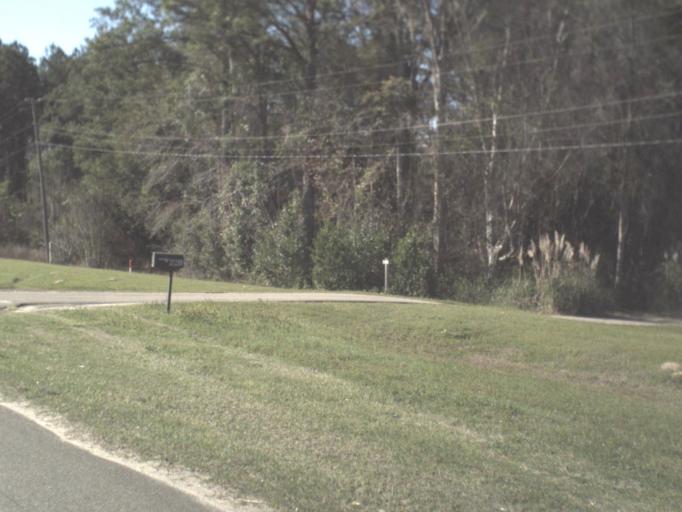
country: US
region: Florida
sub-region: Calhoun County
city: Blountstown
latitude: 30.4432
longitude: -85.0355
